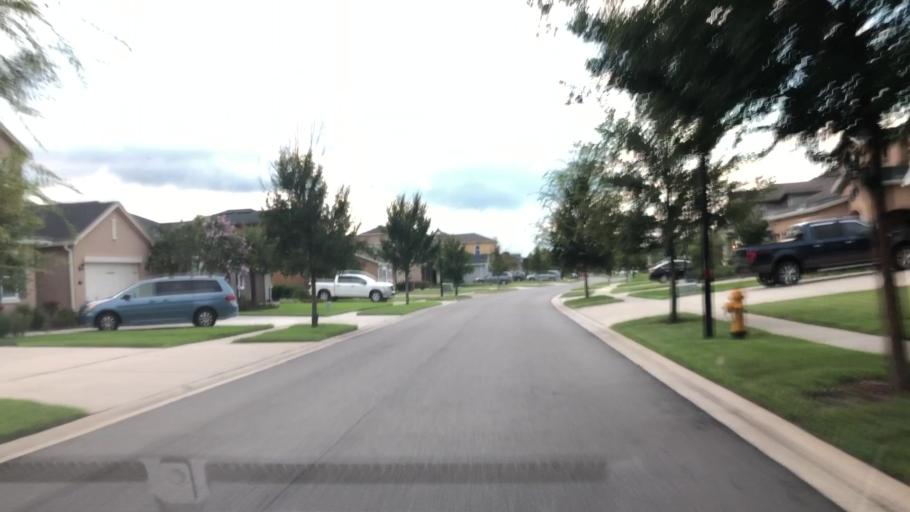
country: US
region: Florida
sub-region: Saint Johns County
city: Palm Valley
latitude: 30.0955
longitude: -81.4618
